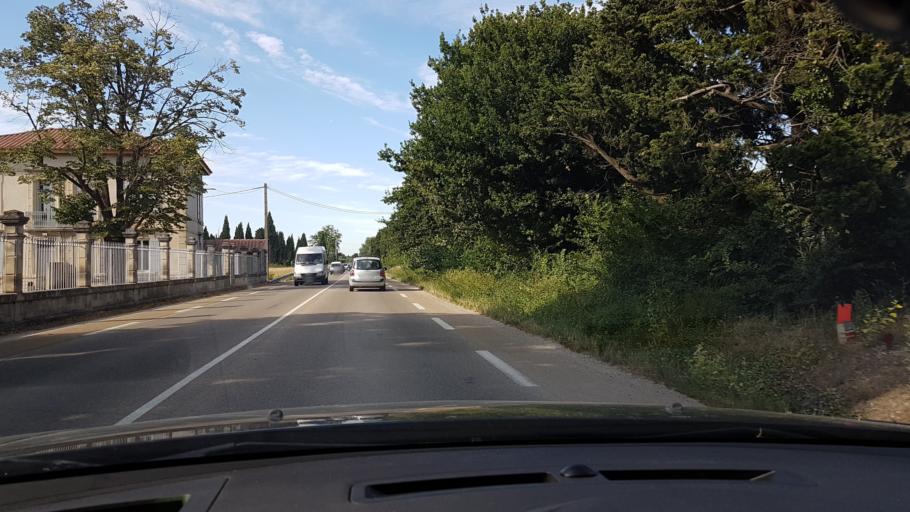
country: FR
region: Provence-Alpes-Cote d'Azur
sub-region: Departement des Bouches-du-Rhone
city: Rognonas
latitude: 43.8913
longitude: 4.7819
